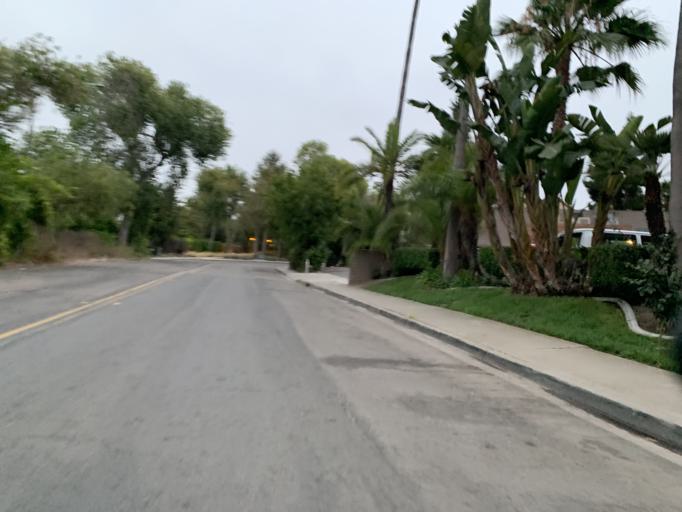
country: US
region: California
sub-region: San Diego County
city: San Diego
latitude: 32.7610
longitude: -117.1881
